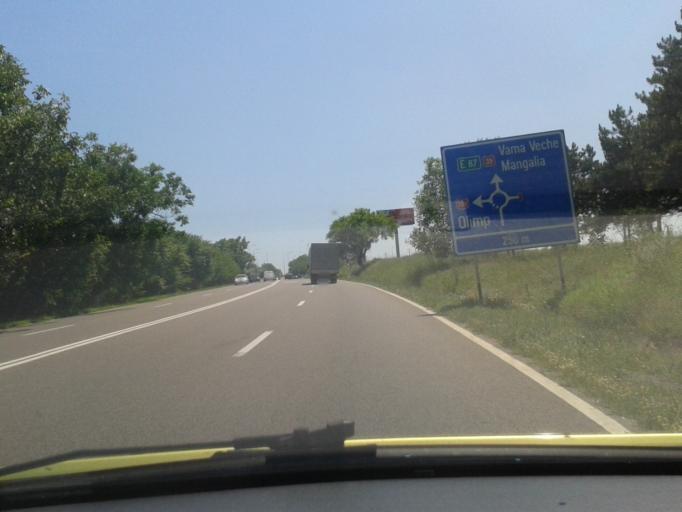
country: RO
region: Constanta
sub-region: Comuna Douazeci si Trei August
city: Douazeci si Trei August
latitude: 43.8995
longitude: 28.5708
